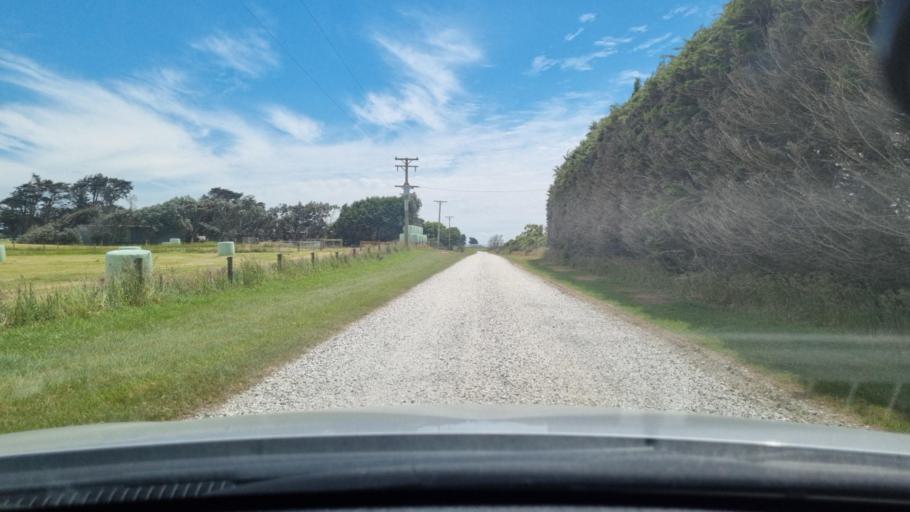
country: NZ
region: Southland
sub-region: Invercargill City
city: Invercargill
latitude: -46.4068
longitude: 168.2598
